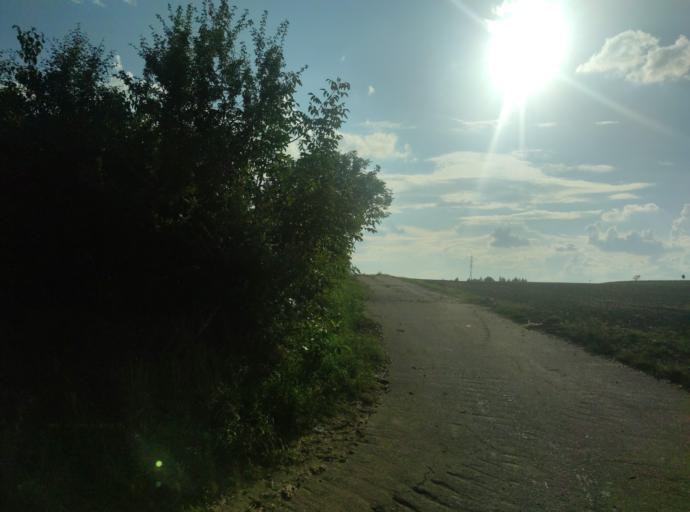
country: CZ
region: South Moravian
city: Vinicne Sumice
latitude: 49.1870
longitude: 16.8406
